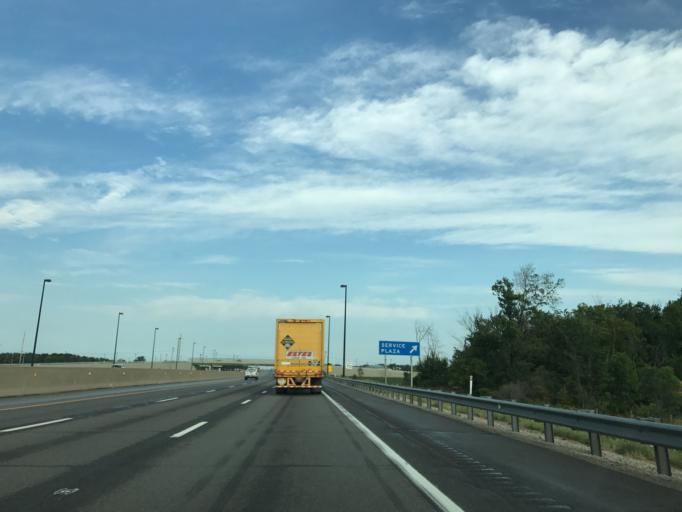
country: US
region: Ohio
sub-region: Sandusky County
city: Clyde
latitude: 41.3667
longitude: -82.9502
